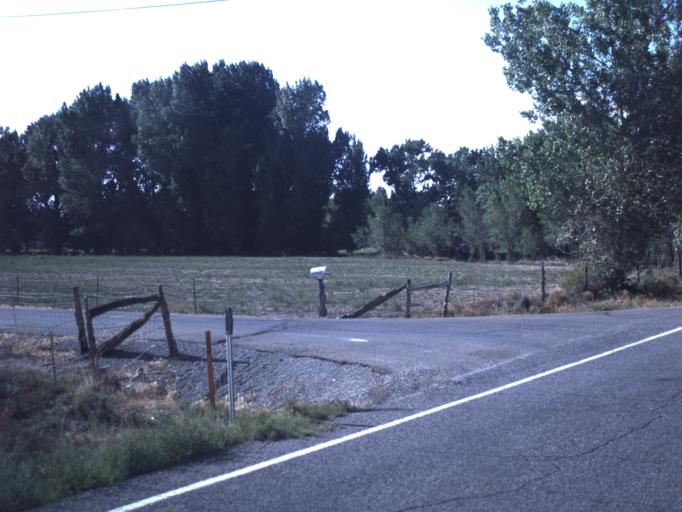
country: US
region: Utah
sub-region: Emery County
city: Huntington
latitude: 39.3556
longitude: -110.8520
